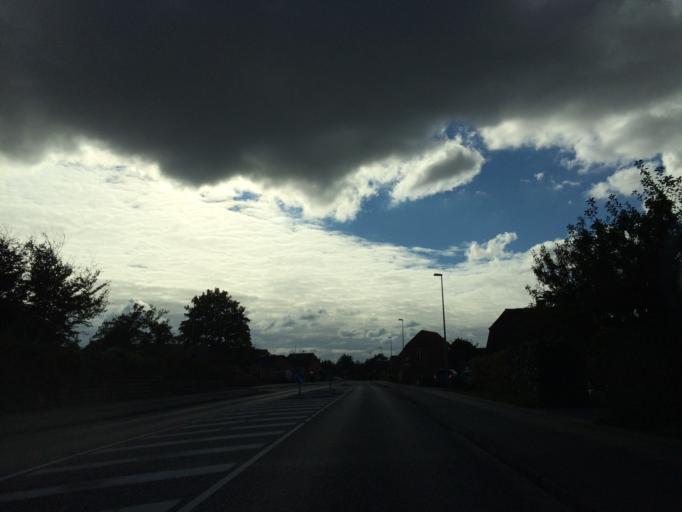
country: DK
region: Central Jutland
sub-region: Skanderborg Kommune
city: Ry
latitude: 56.0948
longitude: 9.7610
